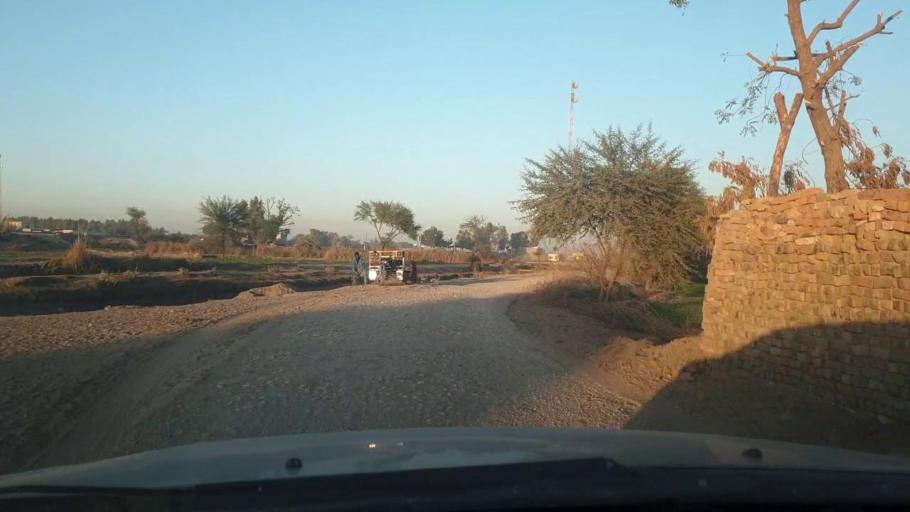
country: PK
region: Sindh
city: Pano Aqil
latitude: 27.9184
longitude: 69.1955
